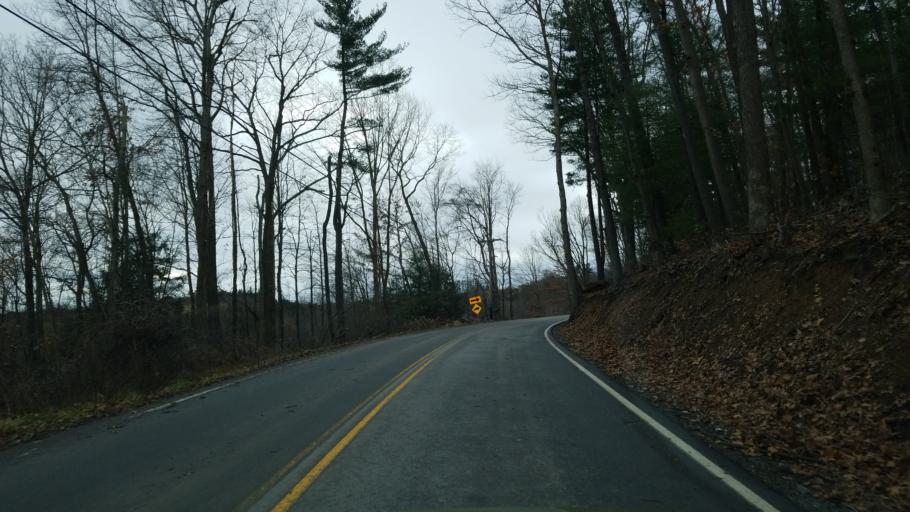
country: US
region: Pennsylvania
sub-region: Clearfield County
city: Clearfield
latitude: 41.0334
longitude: -78.4630
